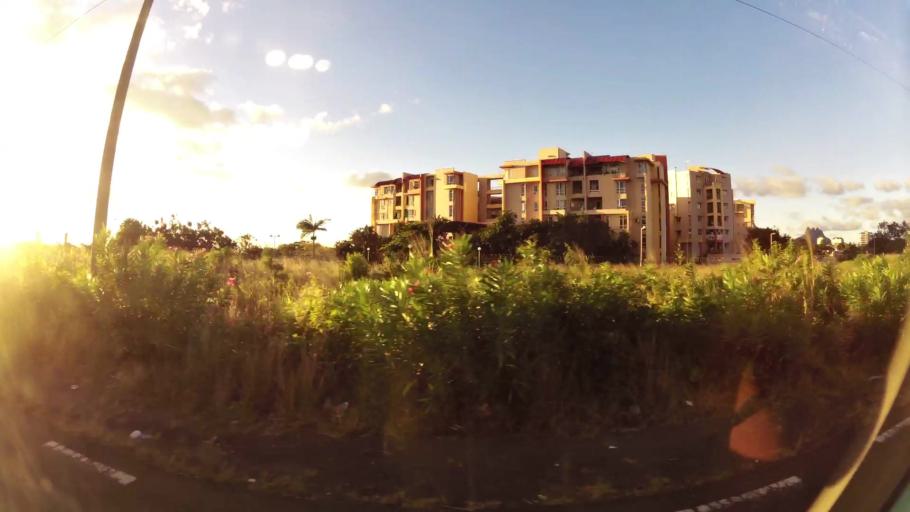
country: MU
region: Plaines Wilhems
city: Ebene
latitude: -20.2416
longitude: 57.4877
